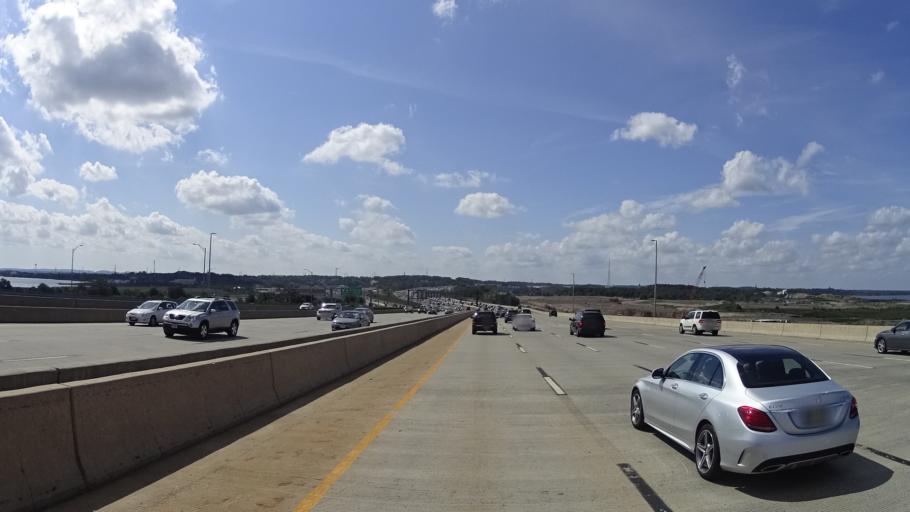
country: US
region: New Jersey
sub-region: Middlesex County
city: Fords
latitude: 40.5057
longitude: -74.3015
